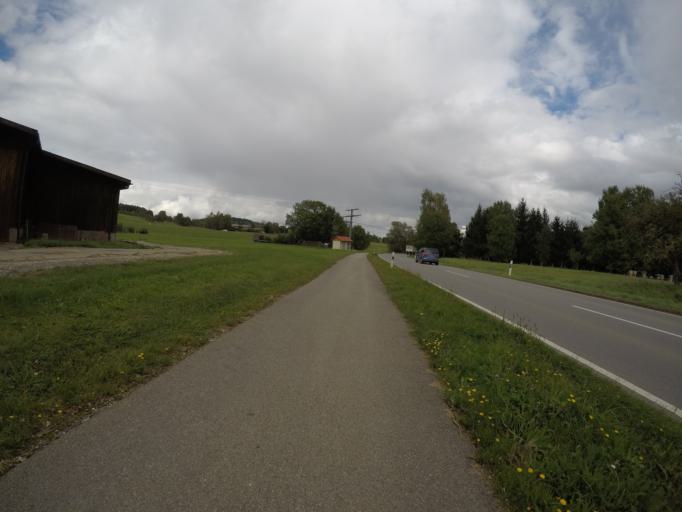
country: DE
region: Baden-Wuerttemberg
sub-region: Tuebingen Region
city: Pfullingen
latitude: 48.4501
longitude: 9.1926
